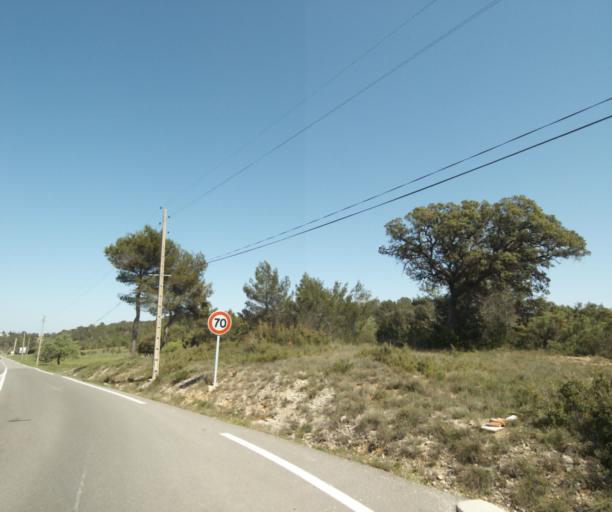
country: FR
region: Languedoc-Roussillon
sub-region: Departement de l'Herault
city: Saint-Drezery
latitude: 43.7228
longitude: 3.9544
